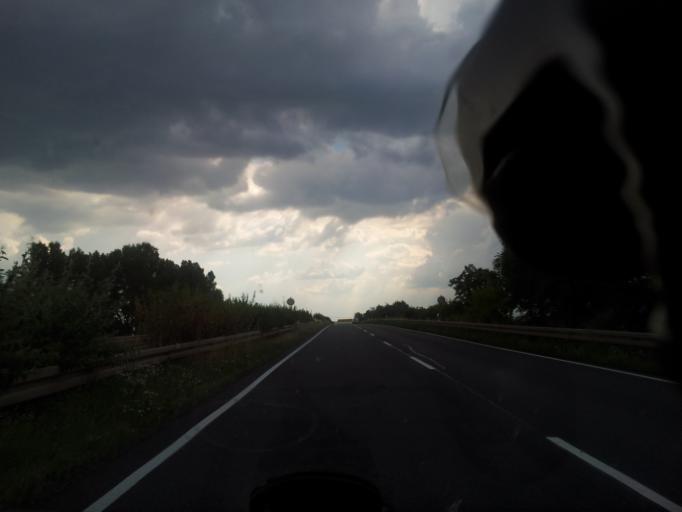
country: DE
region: Saxony-Anhalt
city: Egeln
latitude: 51.9441
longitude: 11.4151
